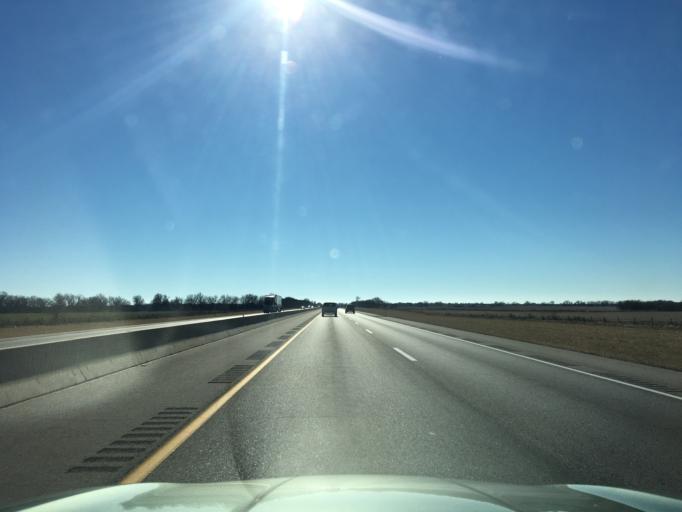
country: US
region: Kansas
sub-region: Sumner County
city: Wellington
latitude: 37.1048
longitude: -97.3388
